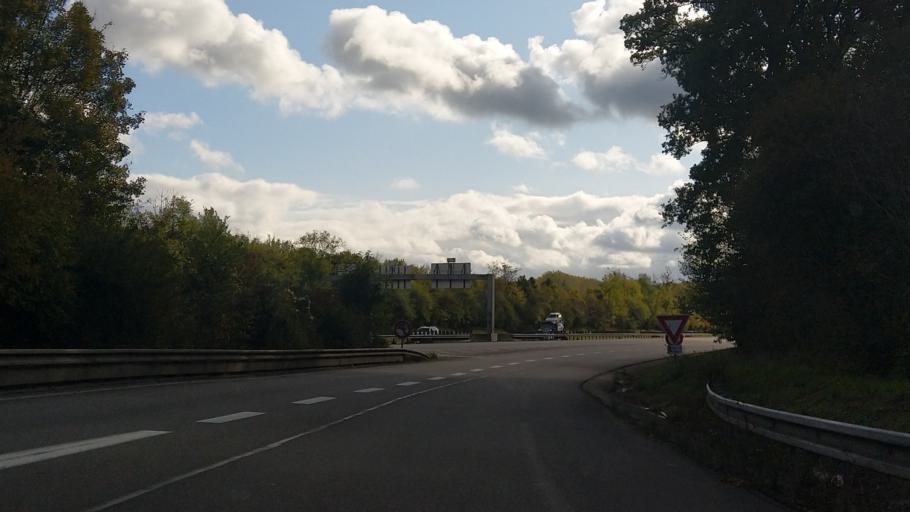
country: FR
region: Ile-de-France
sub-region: Departement du Val-d'Oise
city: Mours
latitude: 49.1237
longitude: 2.2525
